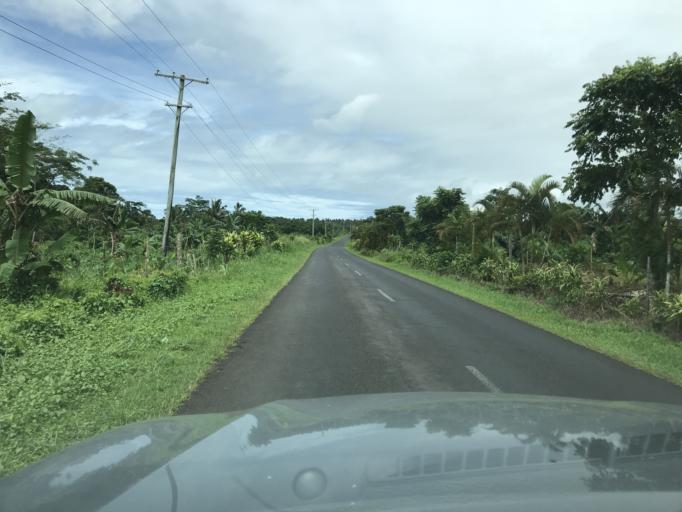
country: WS
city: Nofoali`i
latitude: -13.8747
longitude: -171.9291
